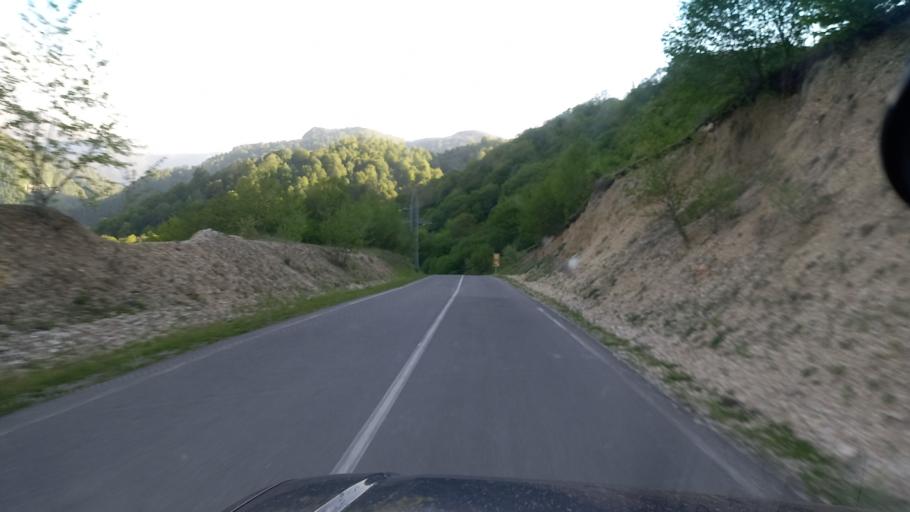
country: RU
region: Ingushetiya
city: Galashki
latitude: 42.9440
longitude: 45.0107
